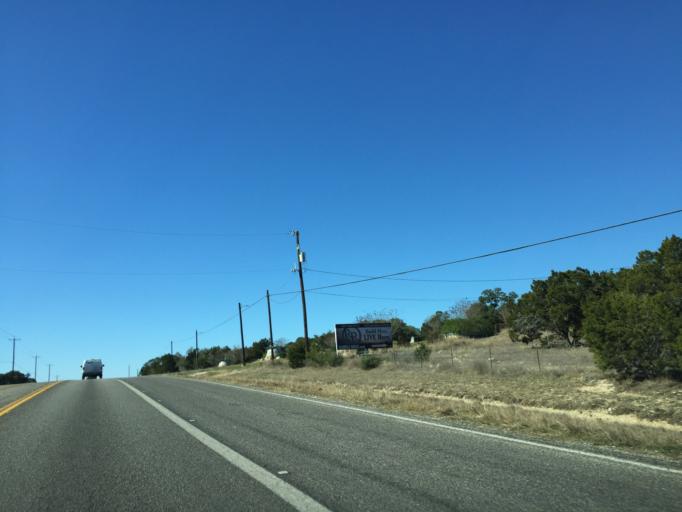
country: US
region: Texas
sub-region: Comal County
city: Garden Ridge
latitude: 29.7000
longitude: -98.3201
